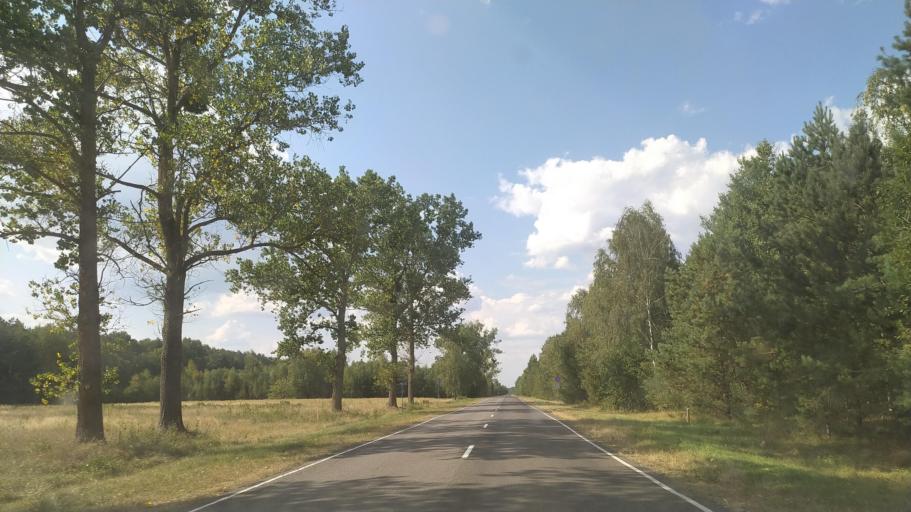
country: BY
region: Brest
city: Drahichyn
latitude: 52.2127
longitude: 25.1348
